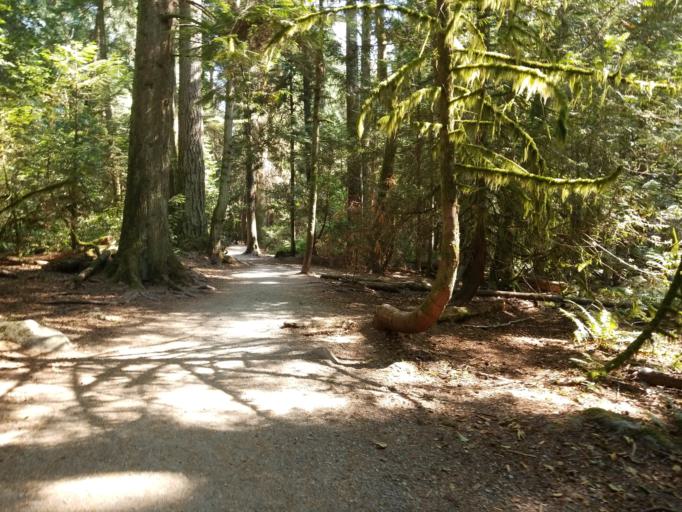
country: CA
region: British Columbia
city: West End
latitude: 49.2515
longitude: -123.2110
